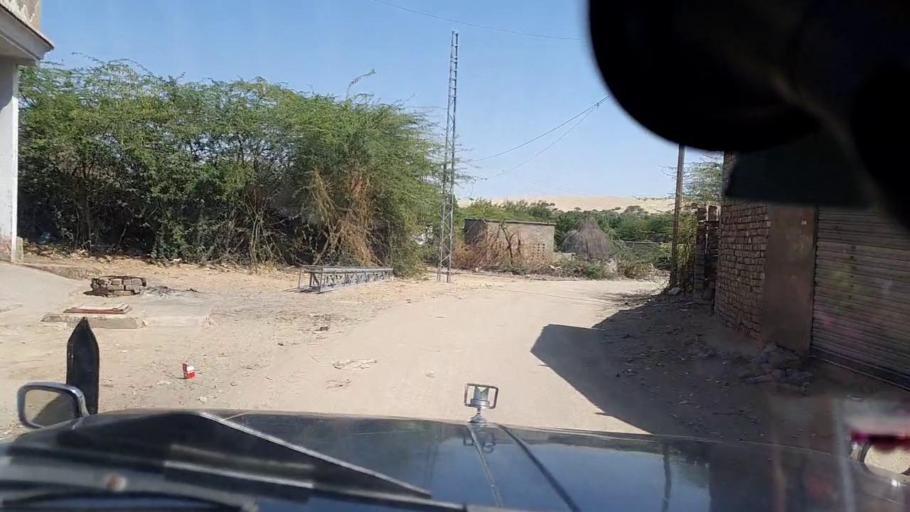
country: PK
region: Sindh
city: Diplo
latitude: 24.4648
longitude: 69.5842
